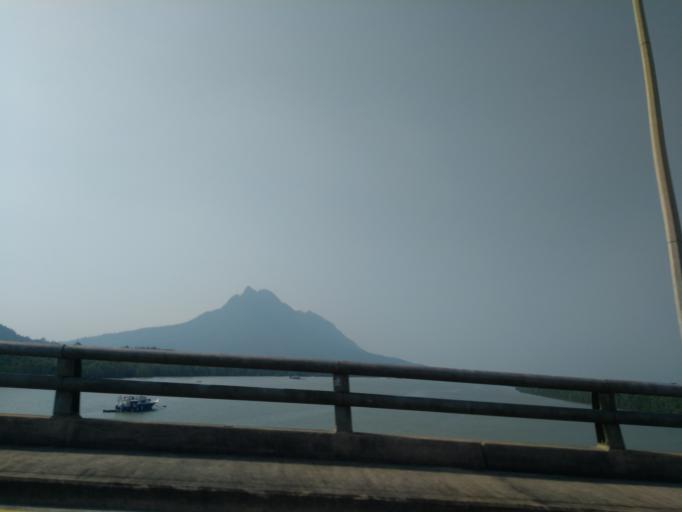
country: MY
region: Sarawak
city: Kuching
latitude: 1.6798
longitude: 110.3387
